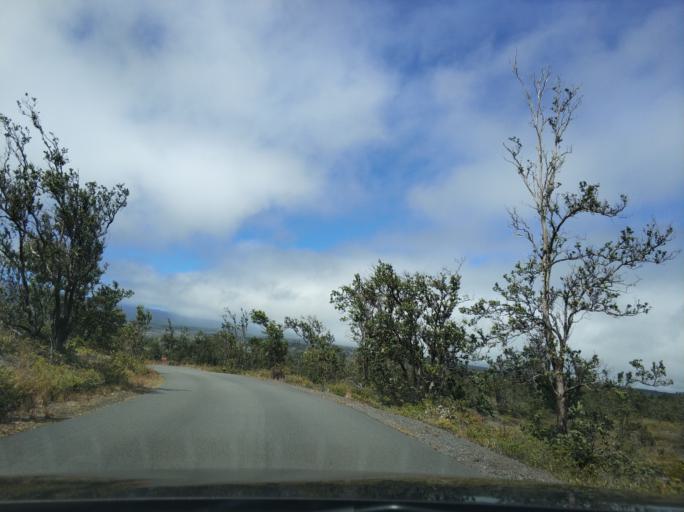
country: US
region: Hawaii
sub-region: Hawaii County
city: Volcano
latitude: 19.4250
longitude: -155.2855
